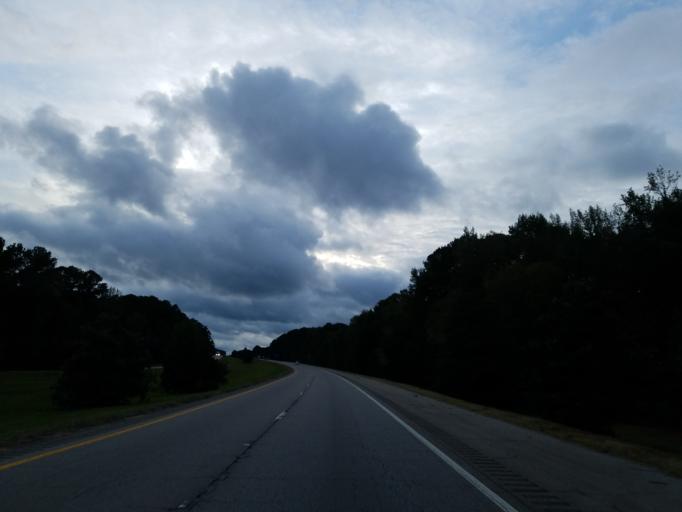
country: US
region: Mississippi
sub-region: Lauderdale County
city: Marion
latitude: 32.4137
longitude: -88.5189
